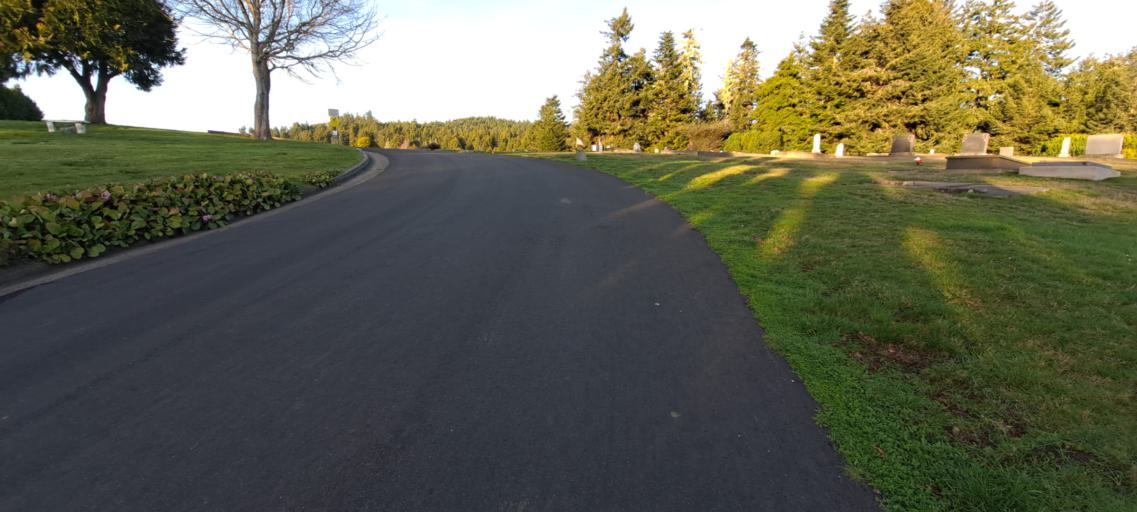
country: US
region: California
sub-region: Humboldt County
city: Fortuna
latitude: 40.5970
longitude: -124.1319
